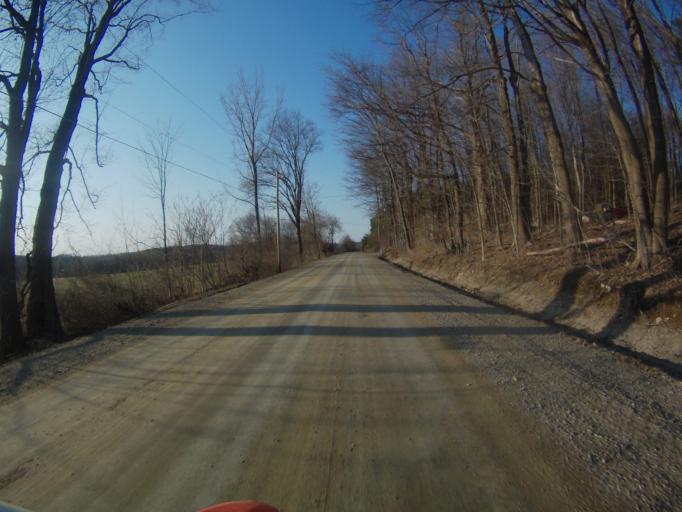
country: US
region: Vermont
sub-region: Addison County
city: Bristol
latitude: 44.1066
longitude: -73.0889
